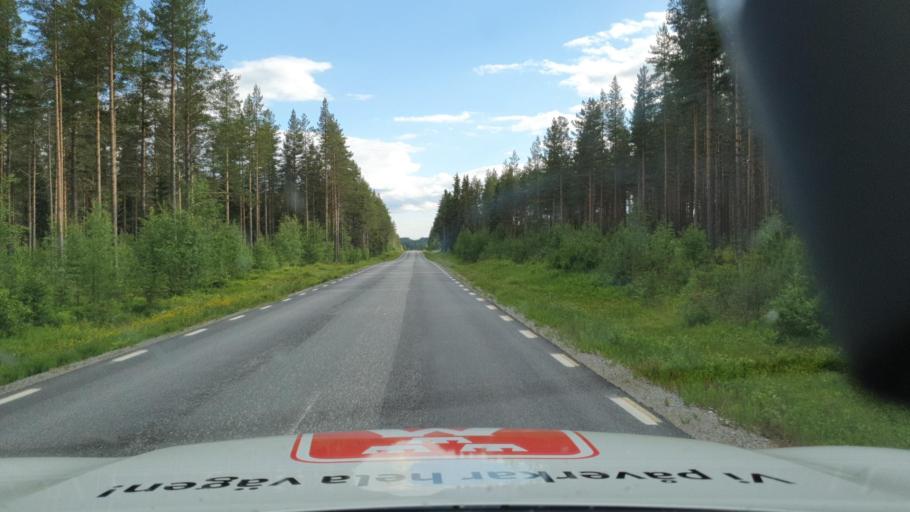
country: SE
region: Vaesterbotten
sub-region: Skelleftea Kommun
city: Langsele
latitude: 64.5919
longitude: 19.9329
